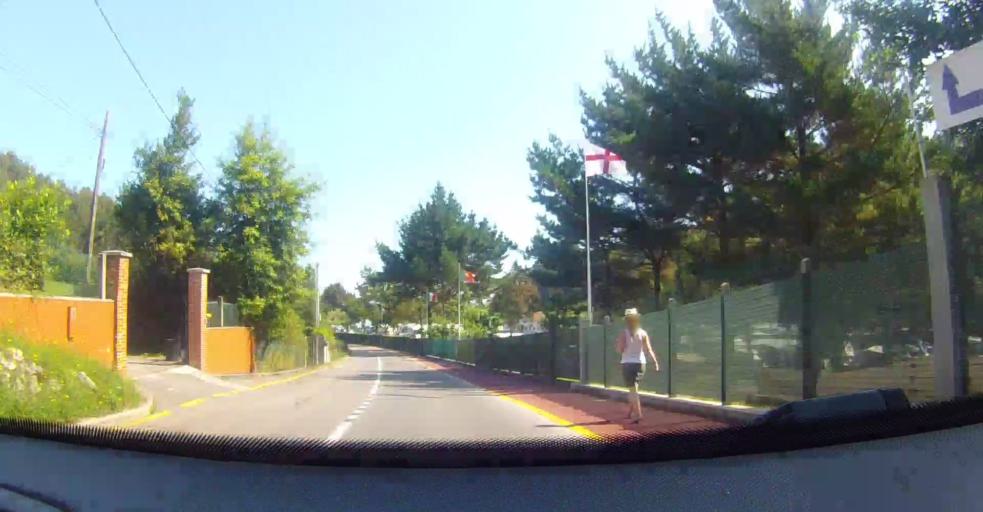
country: ES
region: Asturias
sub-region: Province of Asturias
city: Colunga
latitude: 43.4967
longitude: -5.2642
